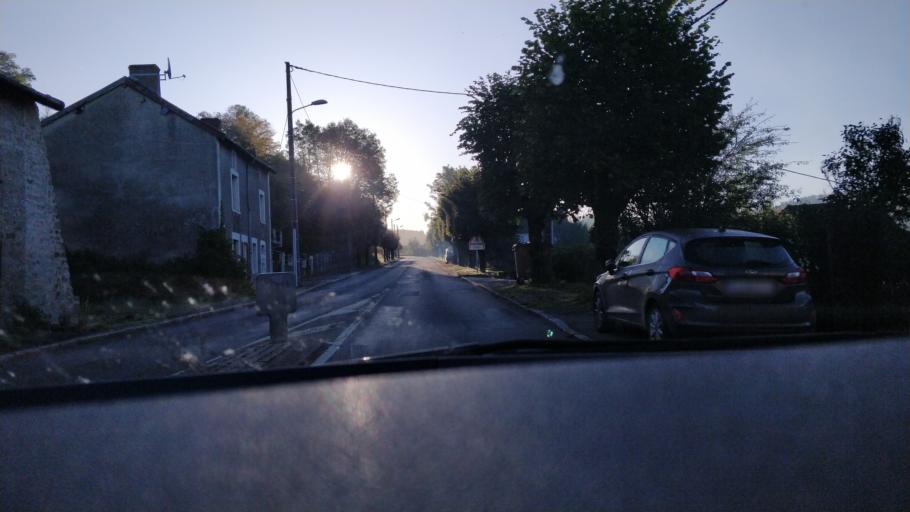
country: FR
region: Limousin
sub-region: Departement de la Creuse
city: Bourganeuf
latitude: 45.9522
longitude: 1.7465
